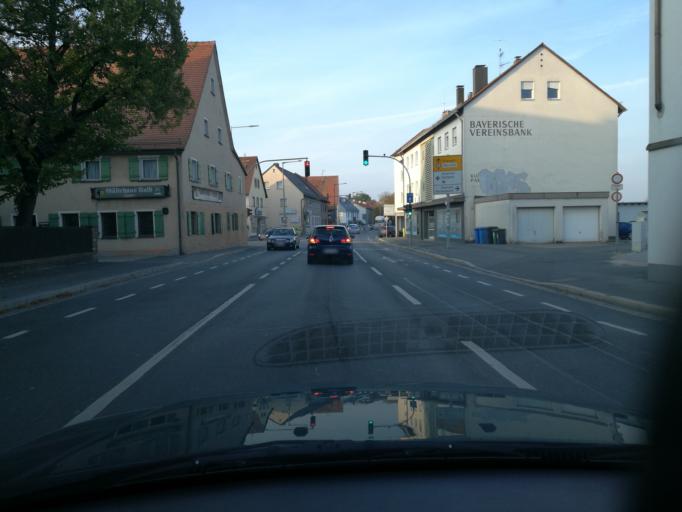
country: DE
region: Bavaria
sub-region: Regierungsbezirk Mittelfranken
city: Furth
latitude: 49.5121
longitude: 10.9750
